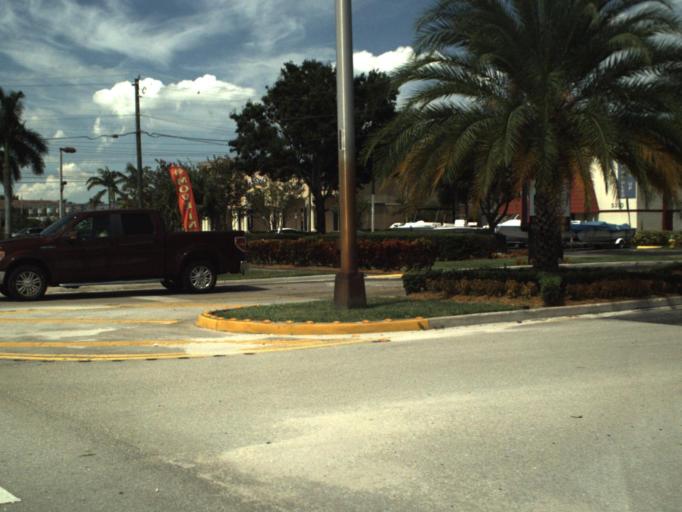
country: US
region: Florida
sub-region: Broward County
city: Cooper City
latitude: 26.0536
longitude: -80.2518
